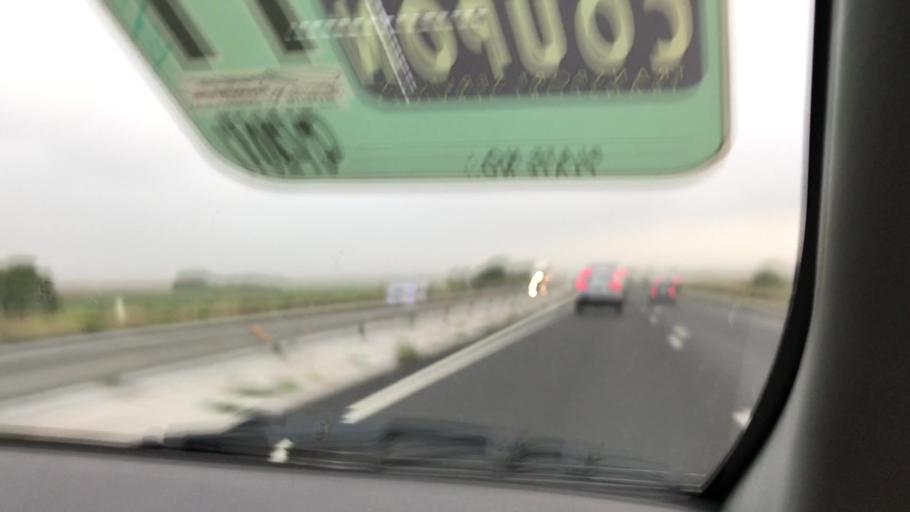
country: PH
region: Central Luzon
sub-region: Province of Tarlac
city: Tinang
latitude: 15.3846
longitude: 120.6599
